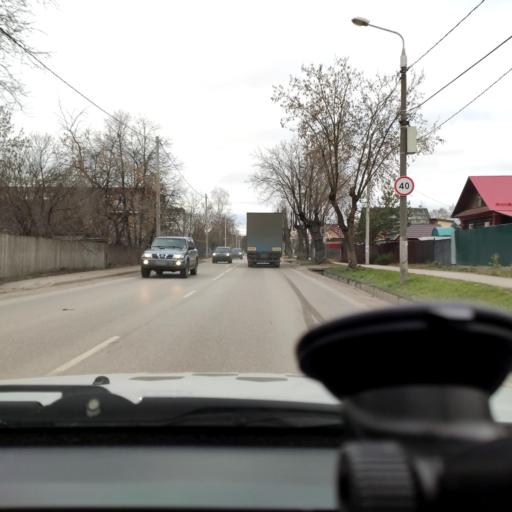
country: RU
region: Perm
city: Perm
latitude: 58.1097
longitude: 56.2967
